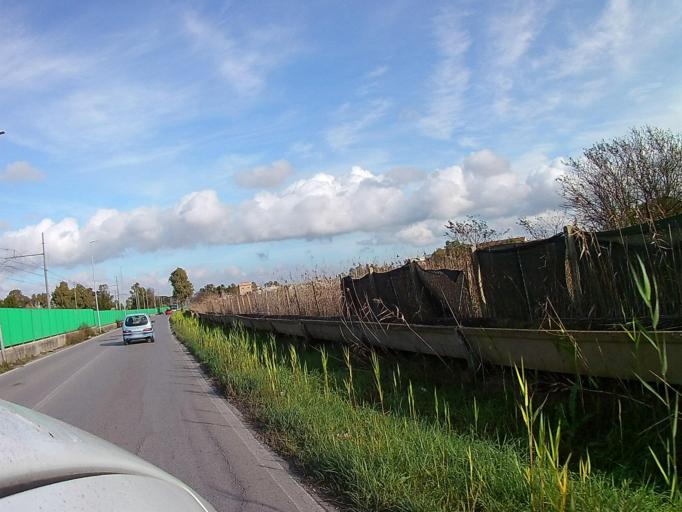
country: IT
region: Latium
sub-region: Citta metropolitana di Roma Capitale
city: Acilia-Castel Fusano-Ostia Antica
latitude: 41.7607
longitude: 12.3088
